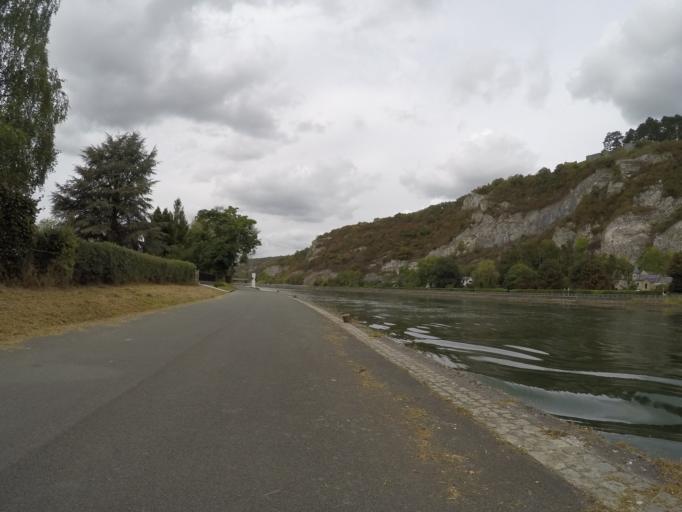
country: BE
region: Wallonia
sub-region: Province de Namur
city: Anhee
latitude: 50.3023
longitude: 4.8957
